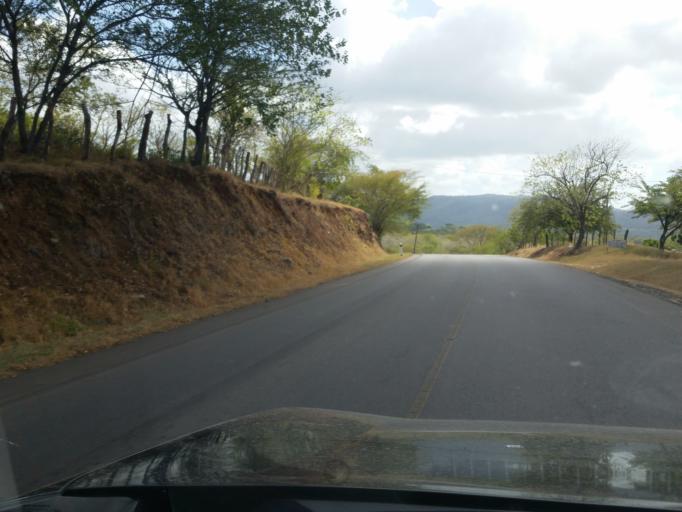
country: NI
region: Chontales
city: Comalapa
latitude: 12.2265
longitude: -85.6438
